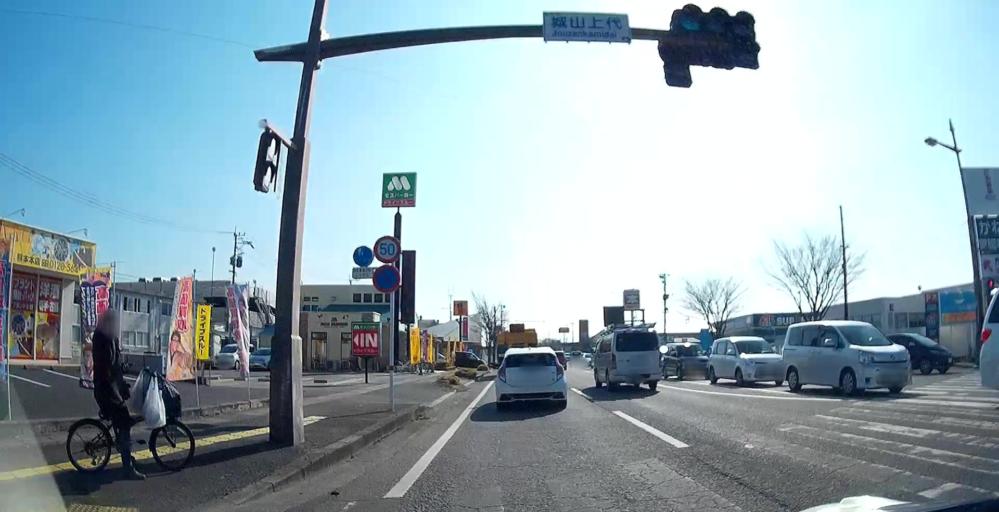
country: JP
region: Kumamoto
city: Kumamoto
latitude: 32.7834
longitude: 130.6734
